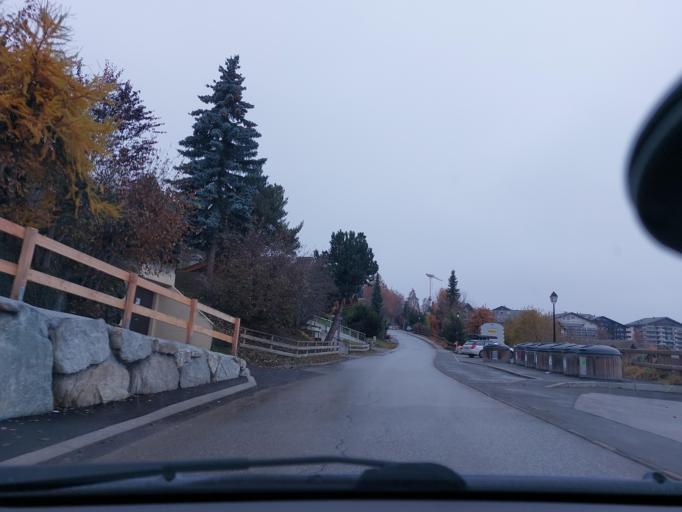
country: CH
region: Valais
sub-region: Conthey District
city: Basse-Nendaz
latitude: 46.1799
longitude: 7.2979
